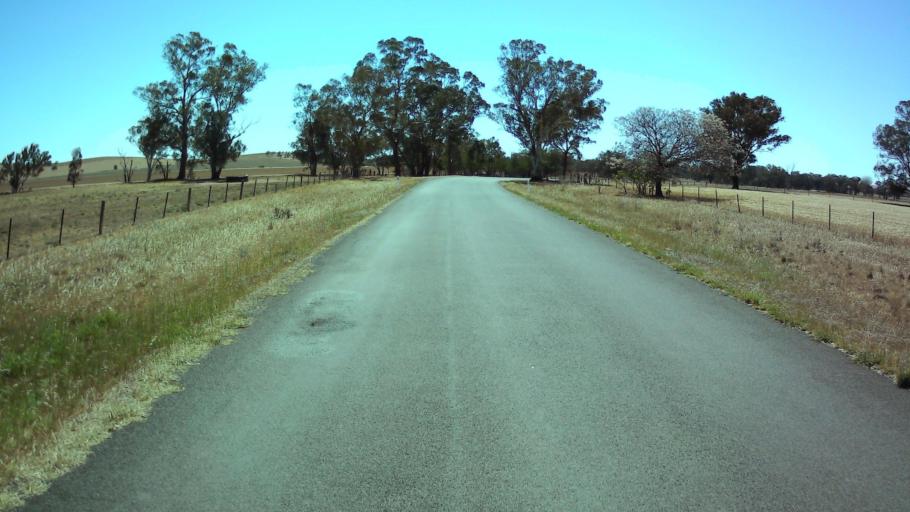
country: AU
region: New South Wales
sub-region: Weddin
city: Grenfell
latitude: -34.0024
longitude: 148.3721
